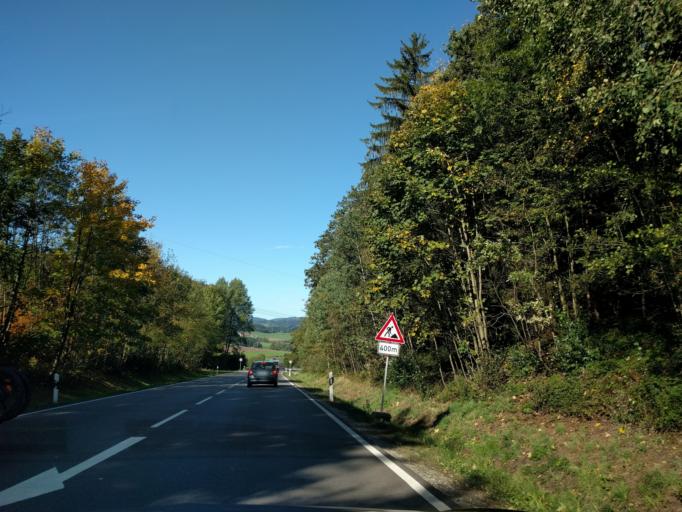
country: DE
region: Bavaria
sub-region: Lower Bavaria
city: Geiersthal
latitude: 49.0357
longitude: 12.9548
